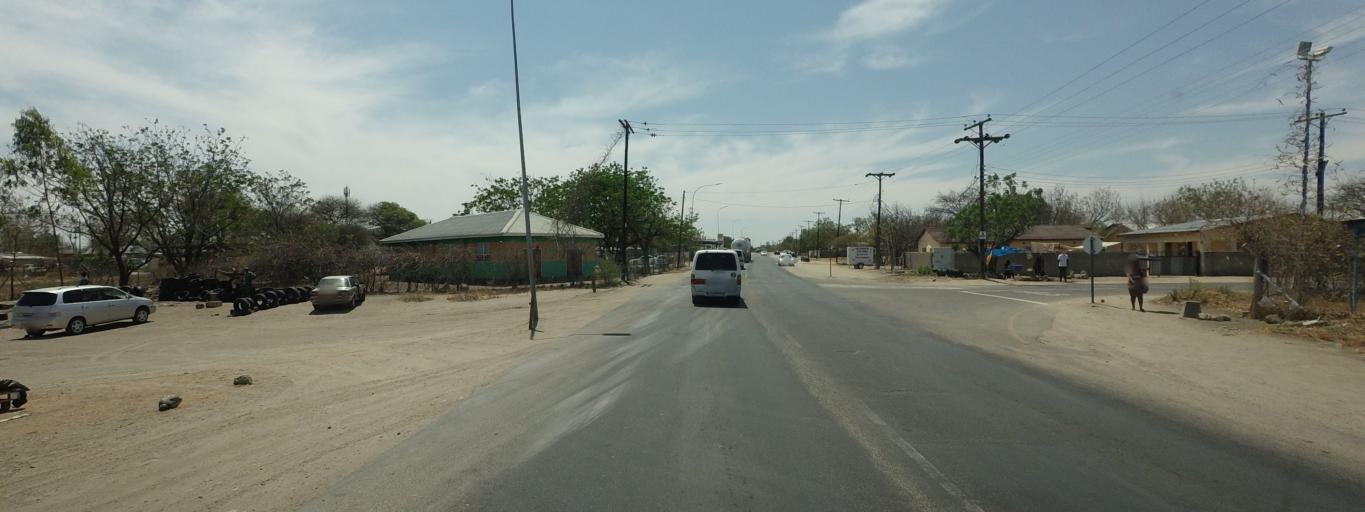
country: BW
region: North East
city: Francistown
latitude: -21.1689
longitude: 27.4959
